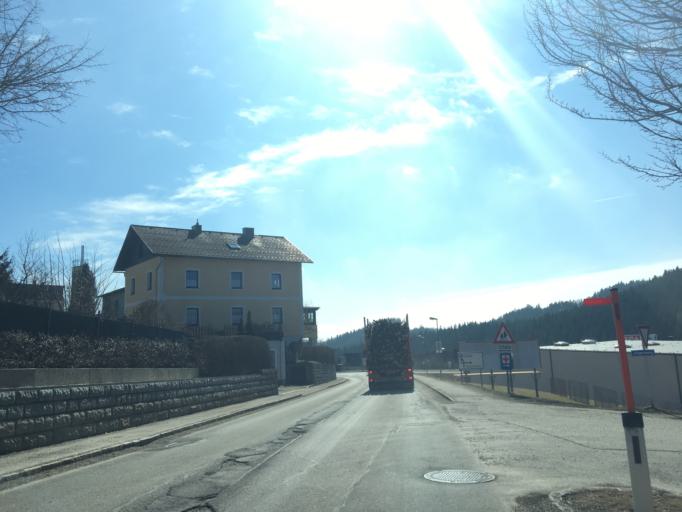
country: AT
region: Upper Austria
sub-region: Politischer Bezirk Perg
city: Sankt Georgen am Walde
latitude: 48.3583
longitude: 14.8970
